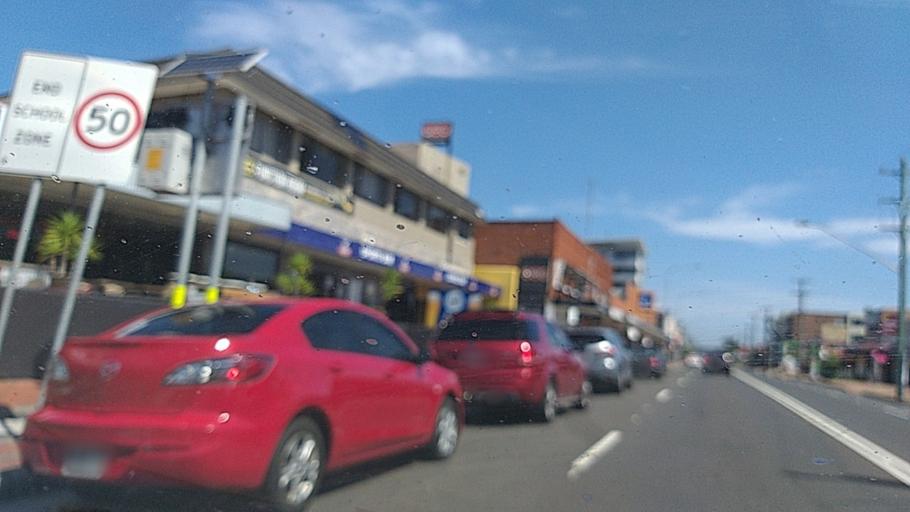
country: AU
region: New South Wales
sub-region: Wollongong
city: Fairy Meadow
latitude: -34.3929
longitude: 150.8932
